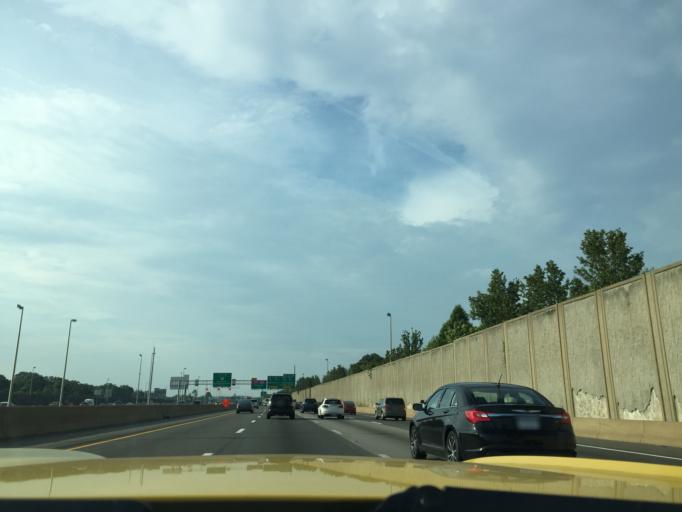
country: US
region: Virginia
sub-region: Fairfax County
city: Newington
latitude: 38.7568
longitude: -77.1833
